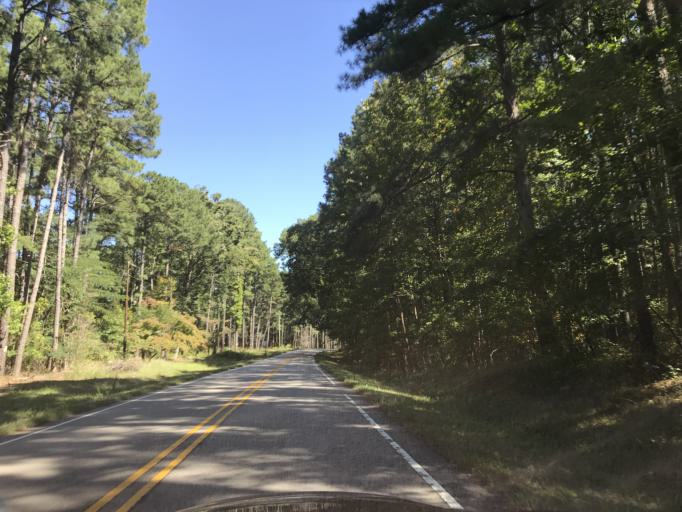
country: US
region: North Carolina
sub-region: Wake County
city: Wake Forest
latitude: 35.9576
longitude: -78.6183
